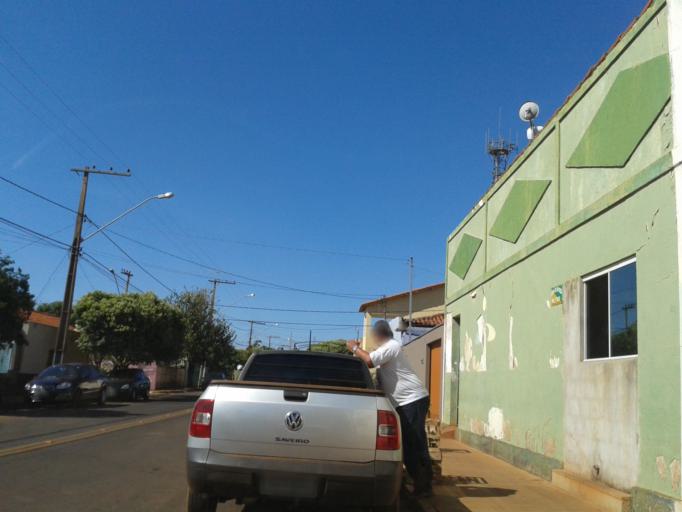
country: BR
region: Minas Gerais
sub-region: Capinopolis
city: Capinopolis
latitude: -18.5143
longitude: -49.5019
